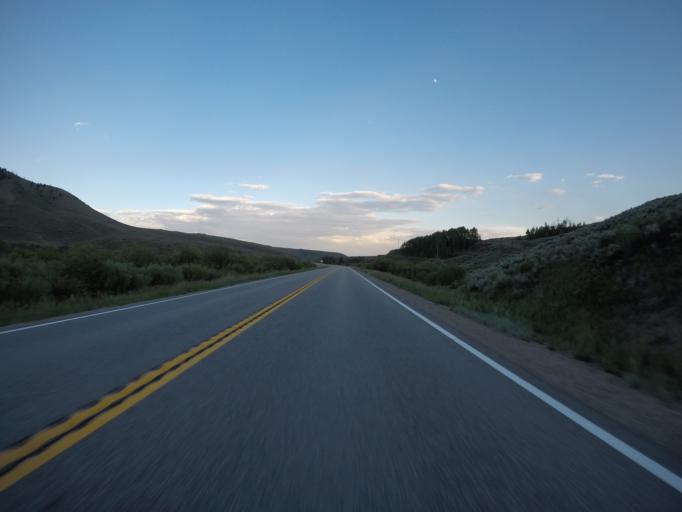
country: US
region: Colorado
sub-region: Grand County
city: Kremmling
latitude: 40.2921
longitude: -106.4825
